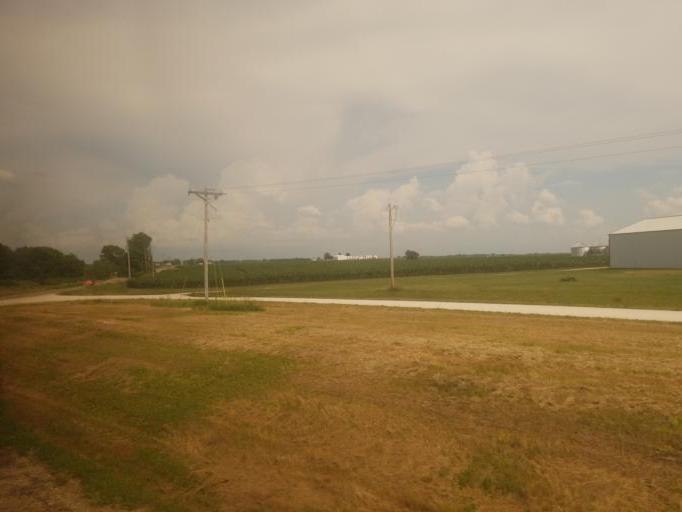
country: US
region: Illinois
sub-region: Knox County
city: Galesburg
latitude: 40.9036
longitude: -90.4391
